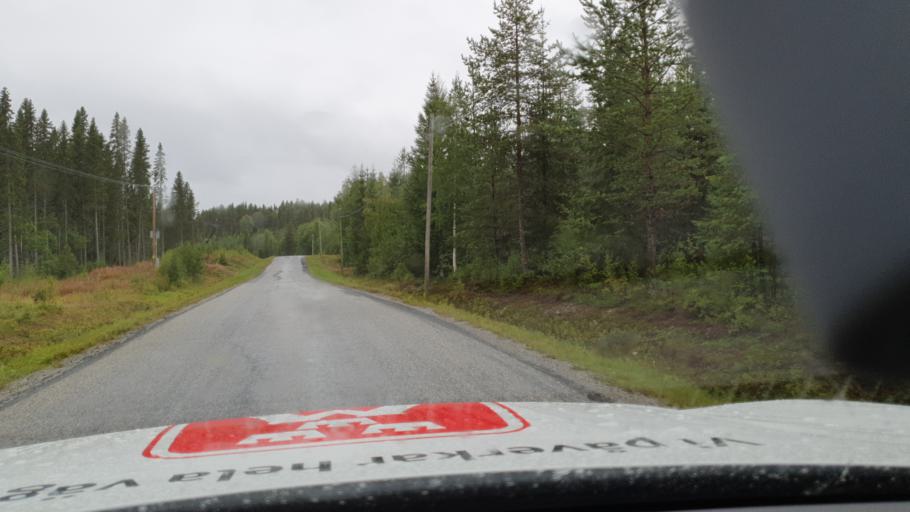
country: SE
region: Vaesterbotten
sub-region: Dorotea Kommun
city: Dorotea
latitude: 64.1302
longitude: 16.2574
